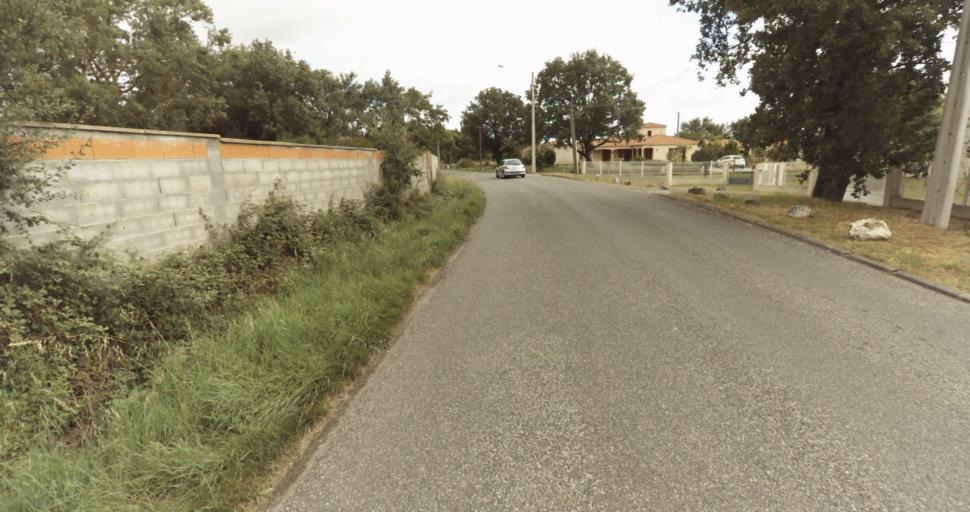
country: FR
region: Midi-Pyrenees
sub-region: Departement de la Haute-Garonne
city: Fonsorbes
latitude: 43.5531
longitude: 1.2272
